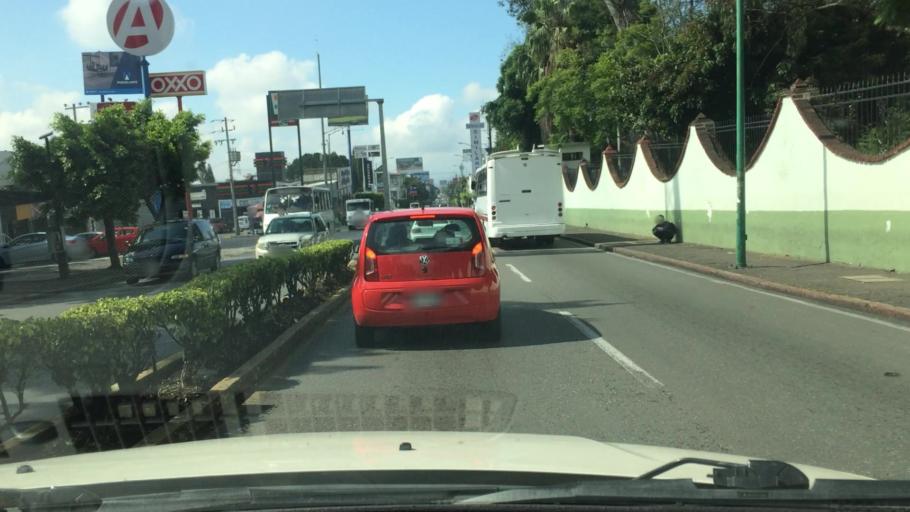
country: MX
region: Morelos
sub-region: Cuernavaca
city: Fraccionamiento Lomas de Ahuatlan
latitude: 18.9621
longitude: -99.2464
